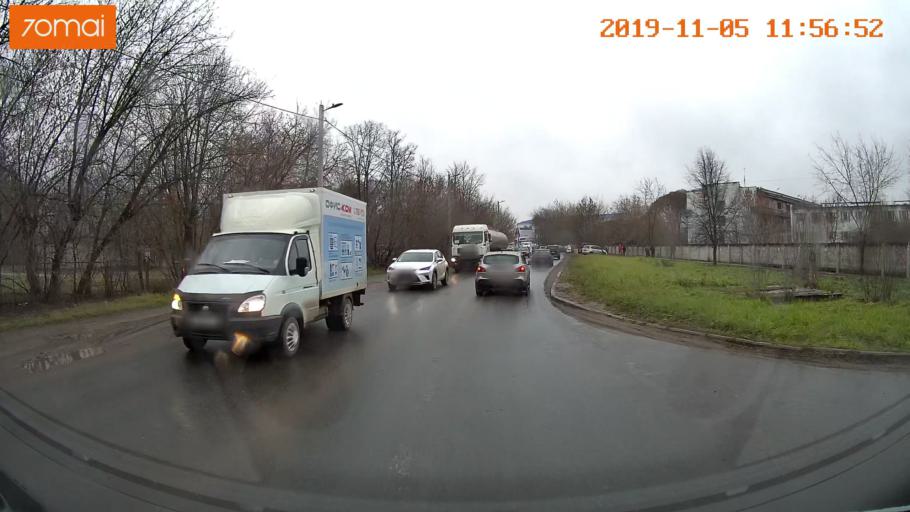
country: RU
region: Ivanovo
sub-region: Gorod Ivanovo
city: Ivanovo
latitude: 56.9853
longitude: 41.0328
